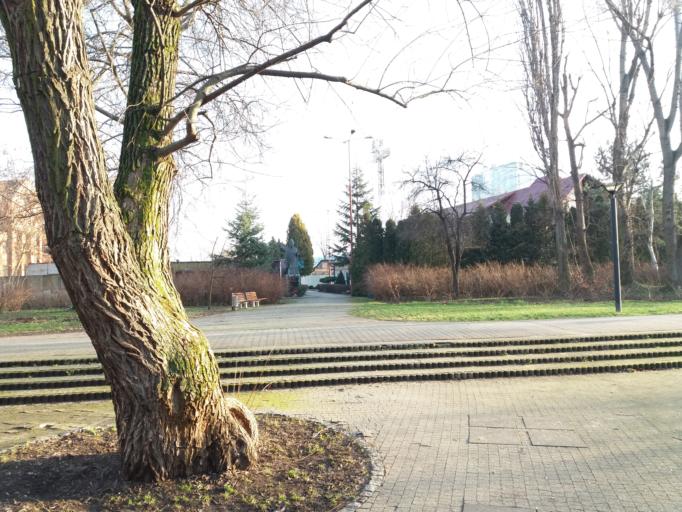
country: PL
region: Masovian Voivodeship
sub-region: Warszawa
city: Zoliborz
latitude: 52.2815
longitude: 20.9798
